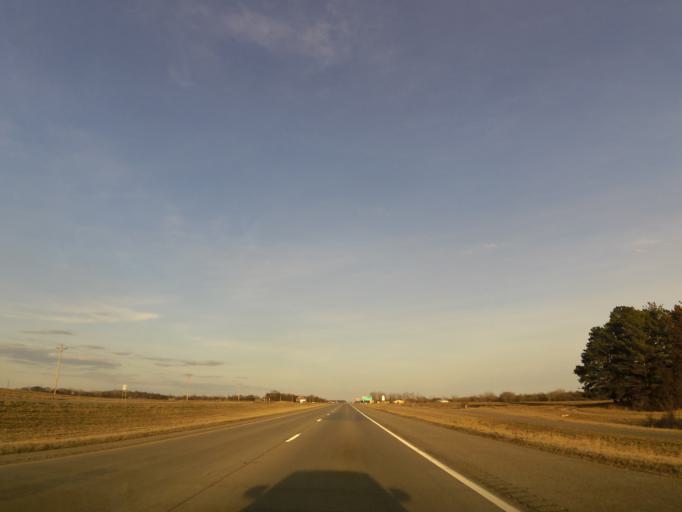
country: US
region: Minnesota
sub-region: McLeod County
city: Glencoe
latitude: 44.7680
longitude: -94.1009
